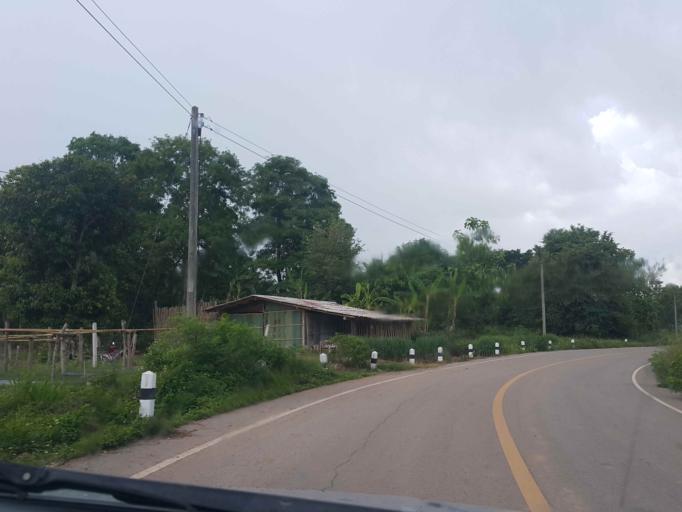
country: TH
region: Phayao
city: Dok Kham Tai
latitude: 19.0358
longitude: 99.9564
